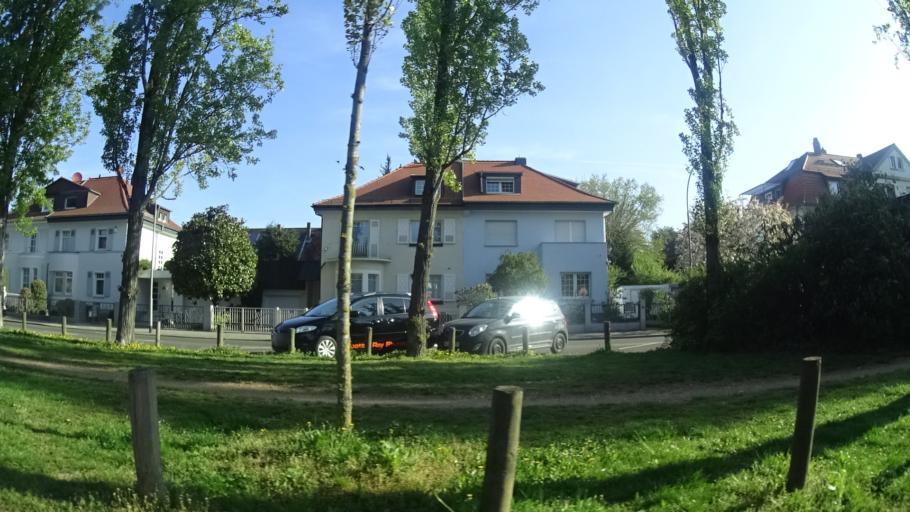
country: DE
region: Hesse
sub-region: Regierungsbezirk Darmstadt
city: Frankfurt am Main
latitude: 50.1384
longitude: 8.6805
